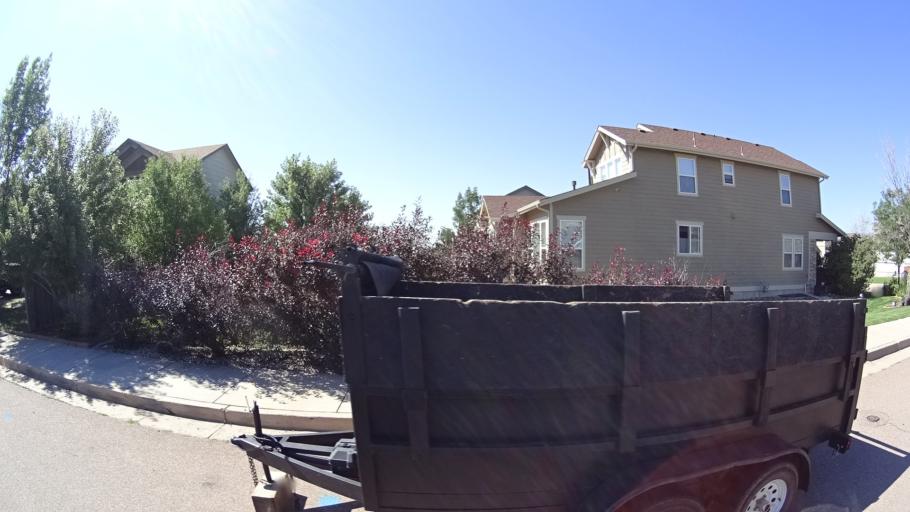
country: US
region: Colorado
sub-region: El Paso County
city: Black Forest
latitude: 38.9438
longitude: -104.7335
